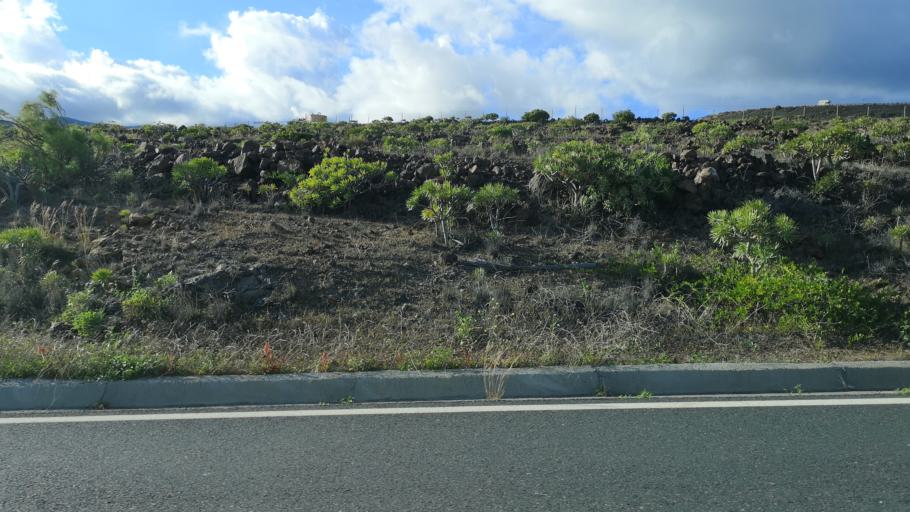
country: ES
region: Canary Islands
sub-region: Provincia de Santa Cruz de Tenerife
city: San Sebastian de la Gomera
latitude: 28.0825
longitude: -17.1418
